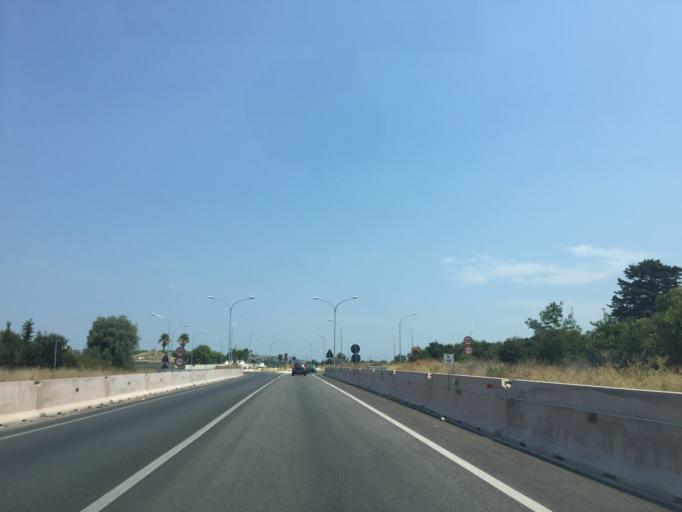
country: IT
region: Sicily
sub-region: Provincia di Siracusa
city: Belvedere
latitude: 37.0728
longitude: 15.2356
